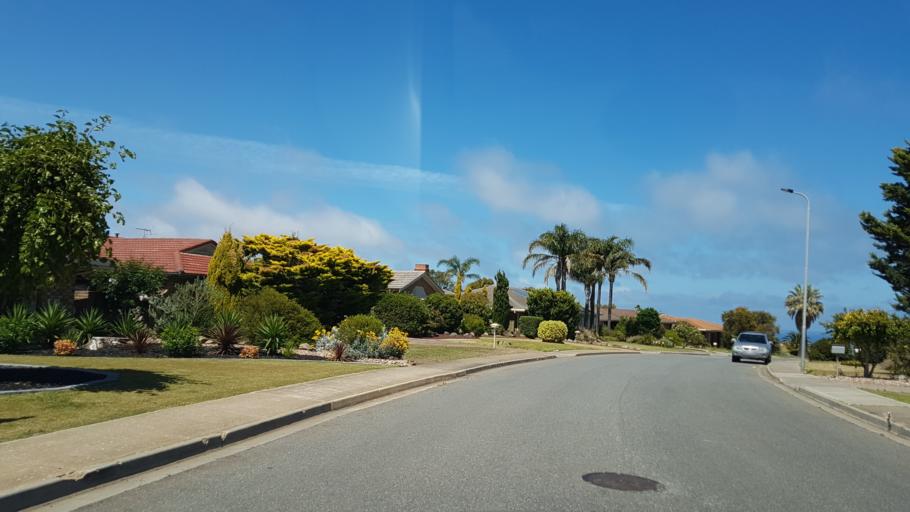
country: AU
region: South Australia
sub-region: Marion
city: Marino
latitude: -35.0646
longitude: 138.5130
